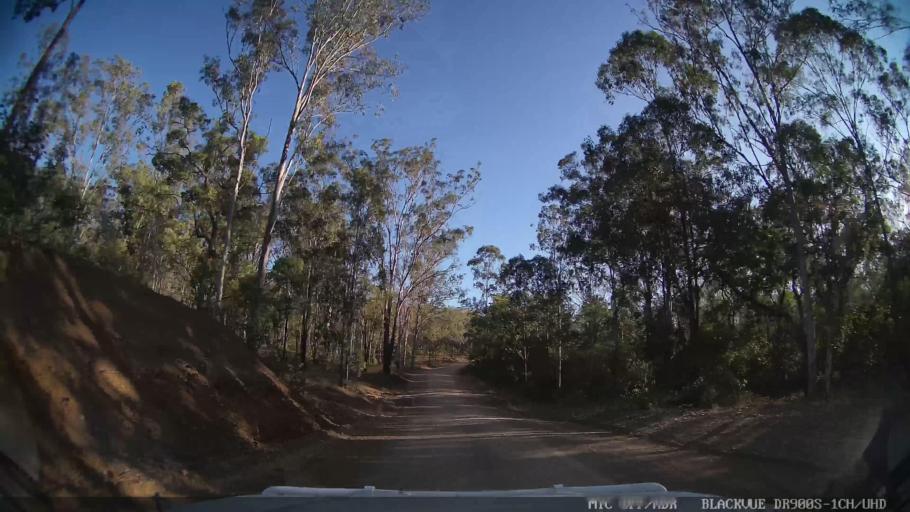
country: AU
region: Queensland
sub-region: Gladstone
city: Toolooa
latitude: -24.6839
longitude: 151.3300
